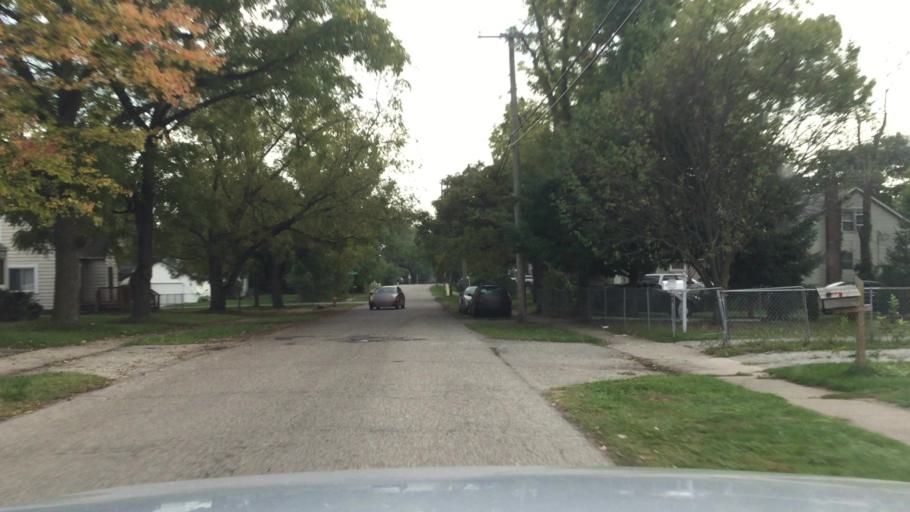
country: US
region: Michigan
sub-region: Oakland County
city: Sylvan Lake
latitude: 42.6320
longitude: -83.3323
